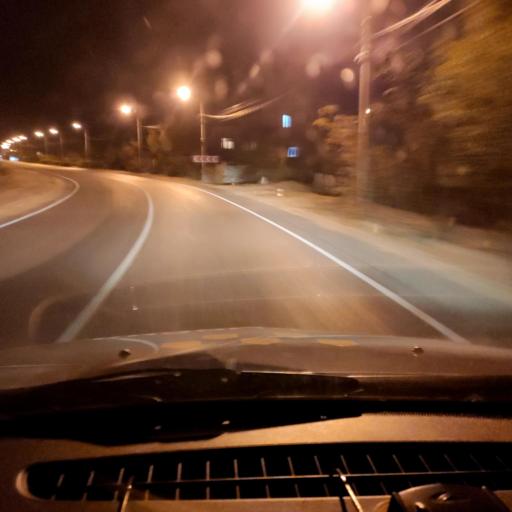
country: RU
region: Voronezj
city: Shilovo
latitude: 51.6031
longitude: 39.0359
